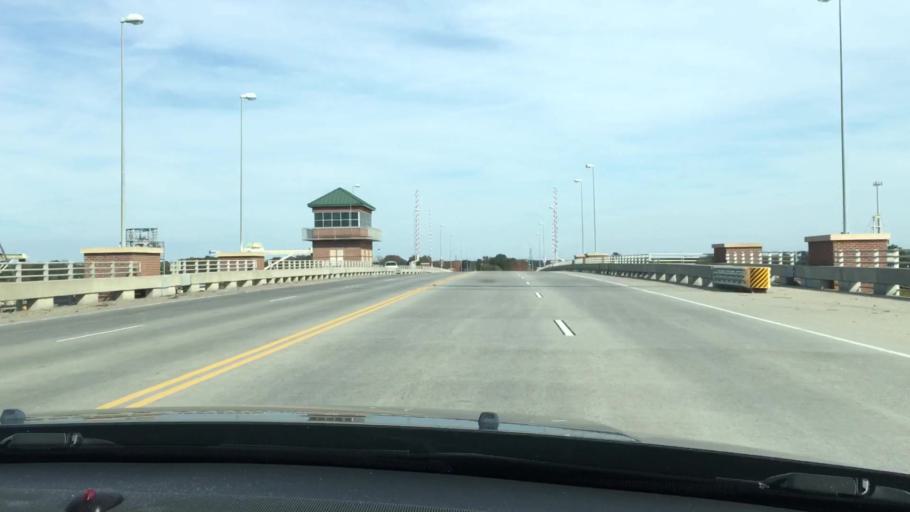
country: US
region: Virginia
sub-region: King William County
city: West Point
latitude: 37.5336
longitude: -76.8068
